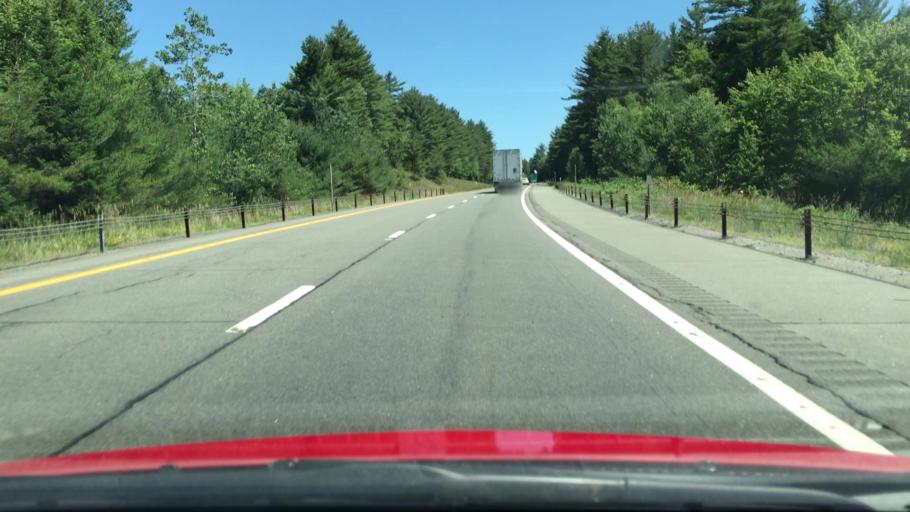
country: US
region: New York
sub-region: Essex County
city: Mineville
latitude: 43.9966
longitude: -73.7206
